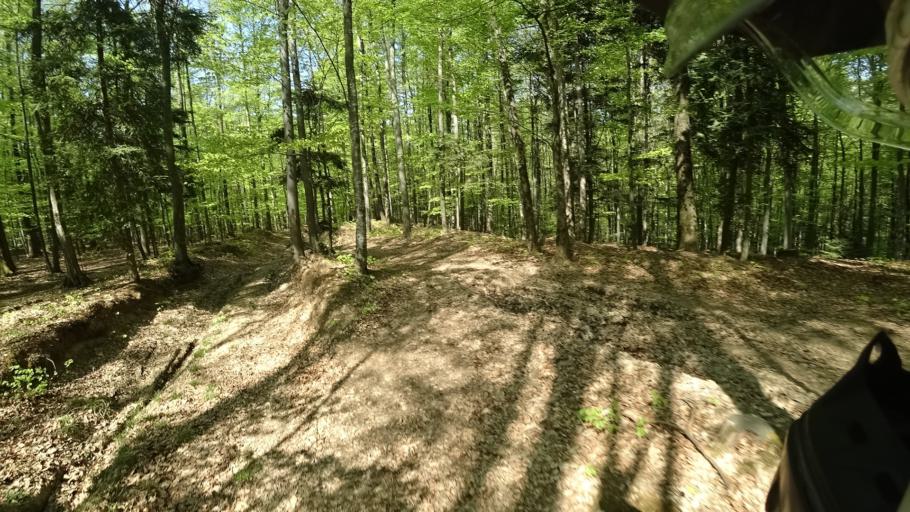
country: HR
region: Zagrebacka
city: Jablanovec
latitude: 45.9066
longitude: 15.9137
